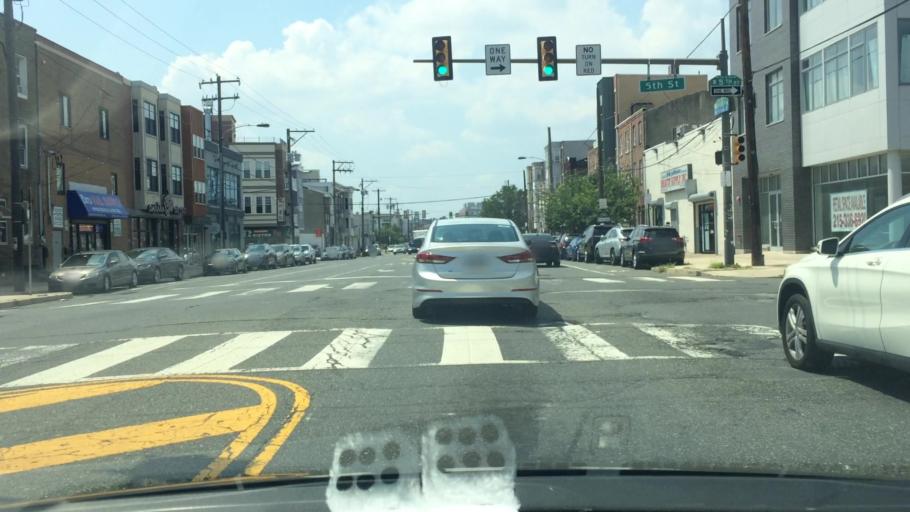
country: US
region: Pennsylvania
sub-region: Philadelphia County
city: Philadelphia
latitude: 39.9347
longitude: -75.1522
